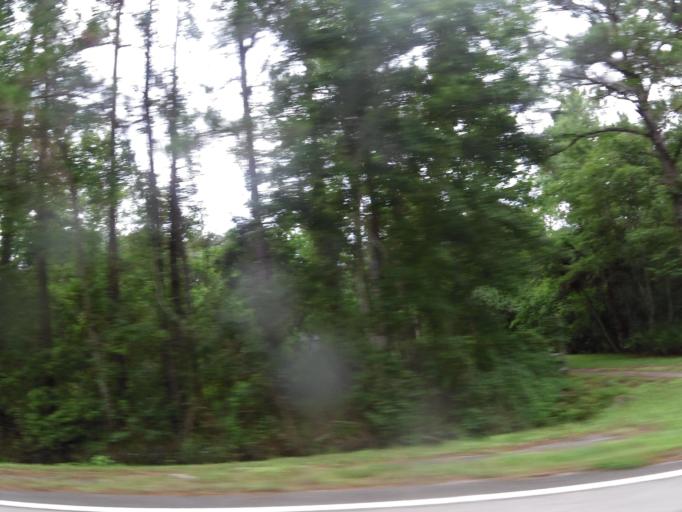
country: US
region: Florida
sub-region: Saint Johns County
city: Saint Augustine South
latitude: 29.8582
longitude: -81.4262
